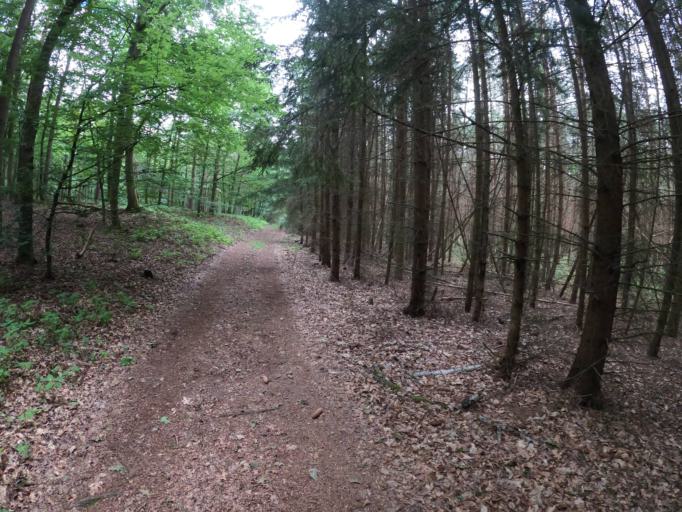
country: DE
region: Brandenburg
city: Angermunde
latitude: 53.0346
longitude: 13.9406
